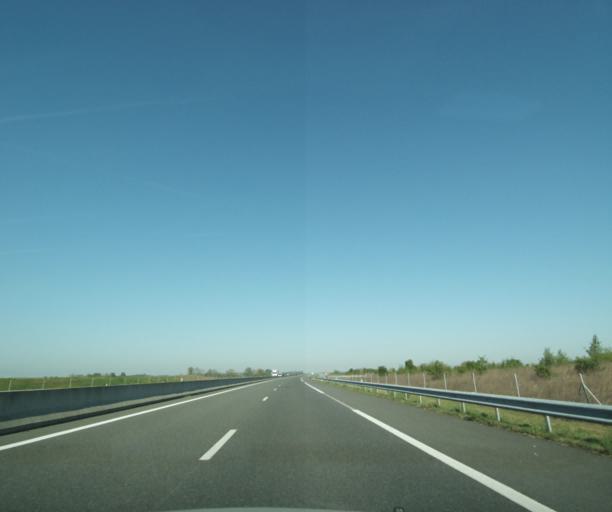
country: FR
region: Centre
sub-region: Departement du Loiret
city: Corbeilles
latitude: 48.0792
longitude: 2.6184
